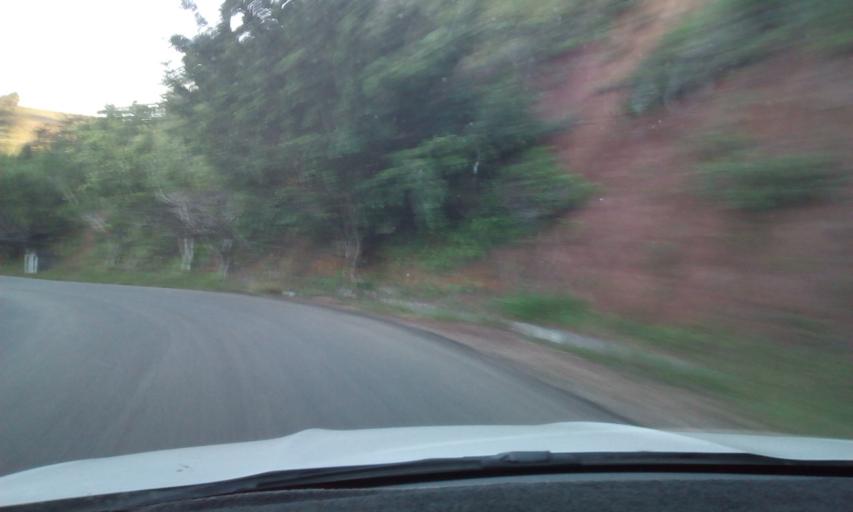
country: BR
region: Paraiba
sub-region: Areia
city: Areia
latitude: -6.9745
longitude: -35.6903
